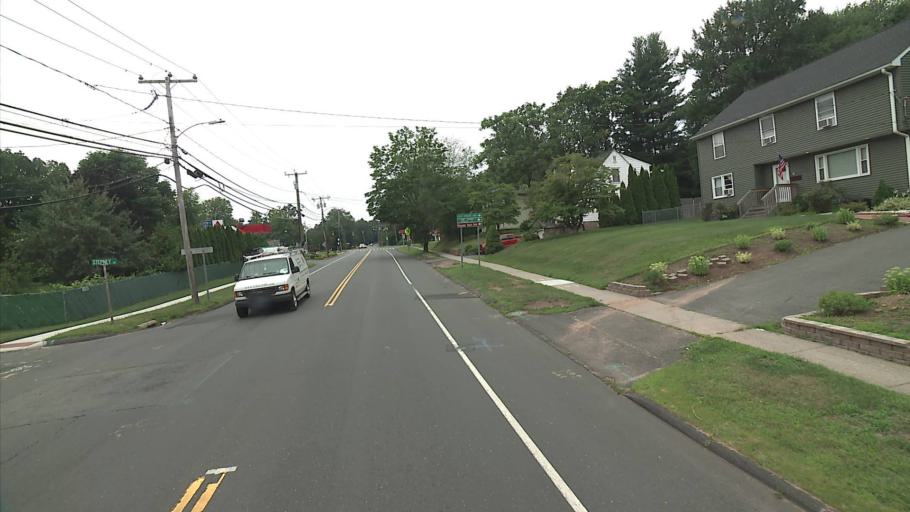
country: US
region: Connecticut
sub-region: Hartford County
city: Wethersfield
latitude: 41.6553
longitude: -72.6405
